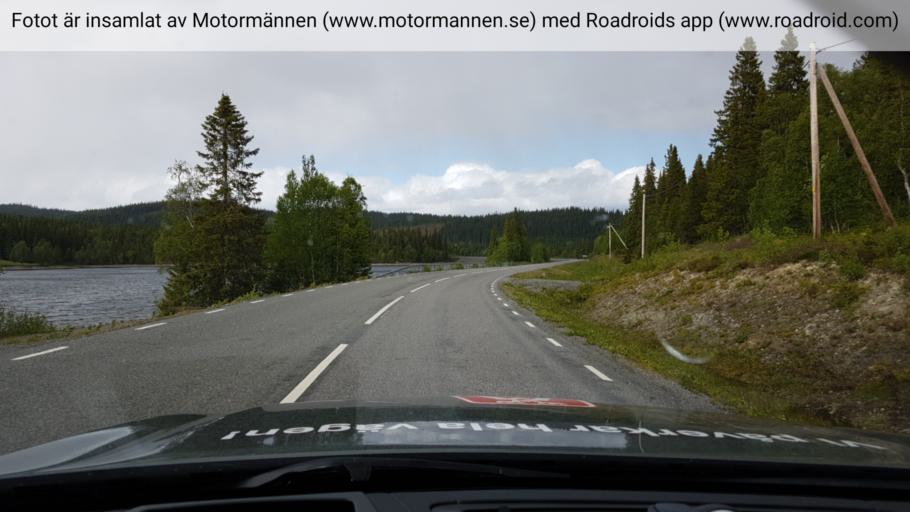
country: SE
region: Jaemtland
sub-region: Are Kommun
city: Are
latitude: 63.6693
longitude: 13.0474
